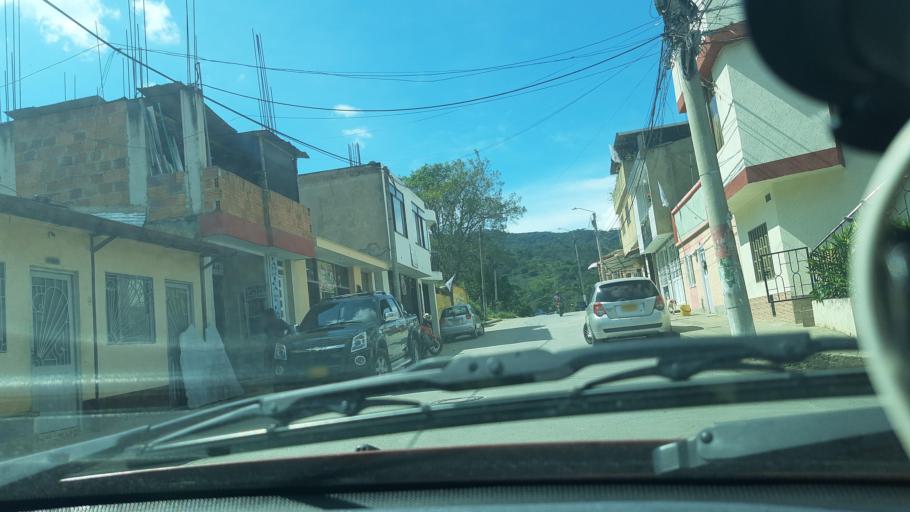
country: CO
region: Boyaca
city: Moniquira
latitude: 5.8761
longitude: -73.5755
